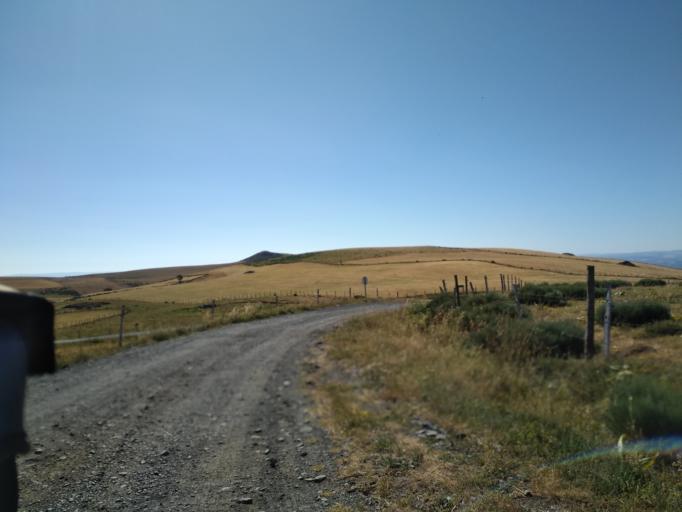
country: FR
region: Auvergne
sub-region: Departement du Cantal
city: Pierrefort
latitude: 45.0195
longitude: 2.8173
